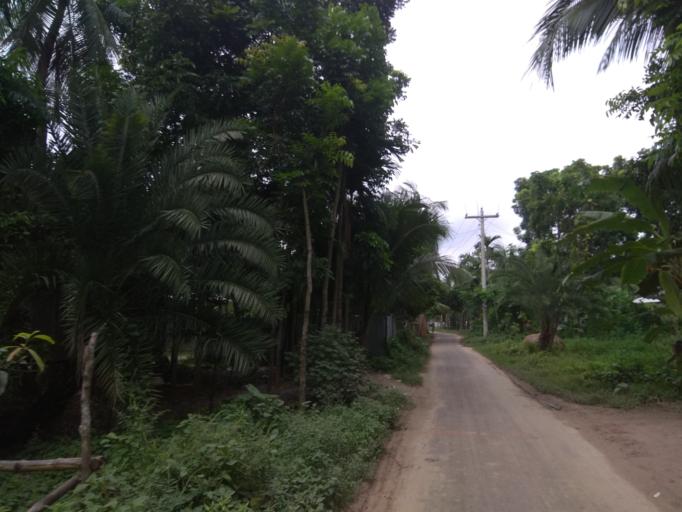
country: BD
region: Dhaka
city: Dohar
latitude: 23.4886
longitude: 89.9885
